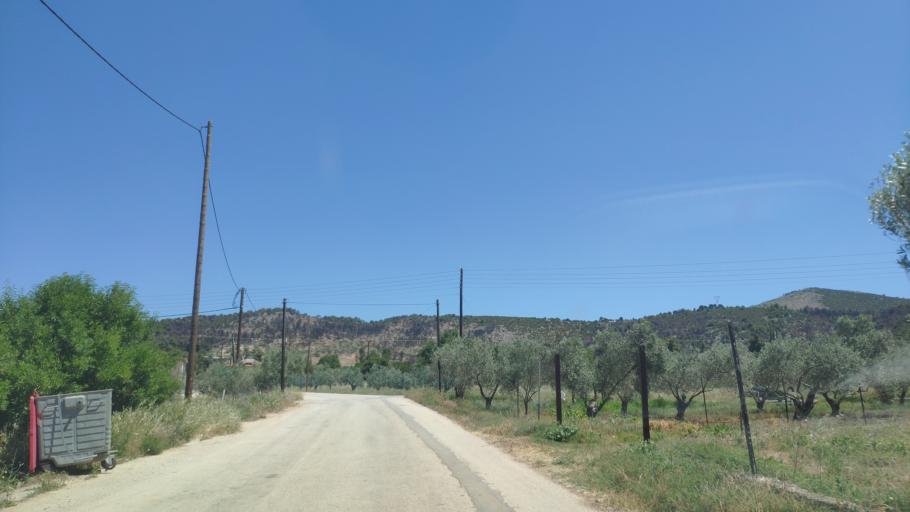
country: GR
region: Peloponnese
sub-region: Nomos Korinthias
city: Athikia
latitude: 37.8234
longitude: 22.9268
